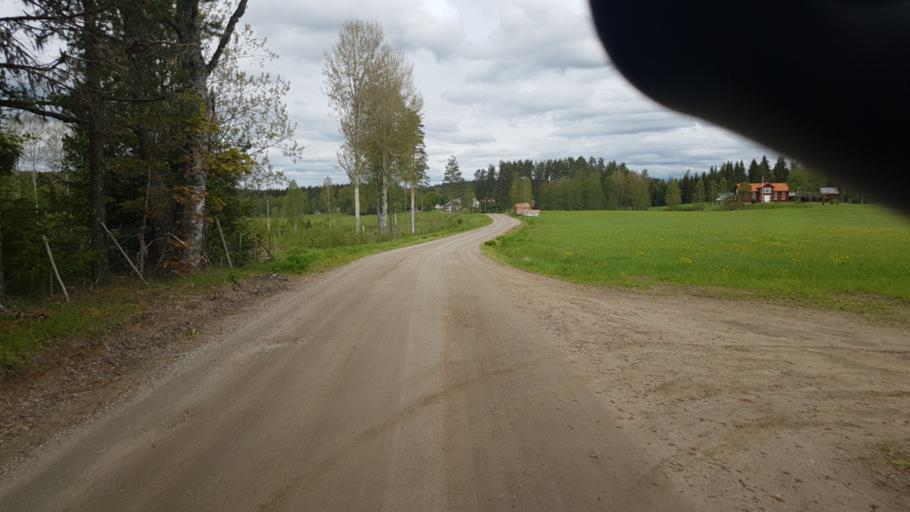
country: SE
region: Vaermland
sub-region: Arvika Kommun
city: Arvika
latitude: 59.8689
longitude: 12.6155
